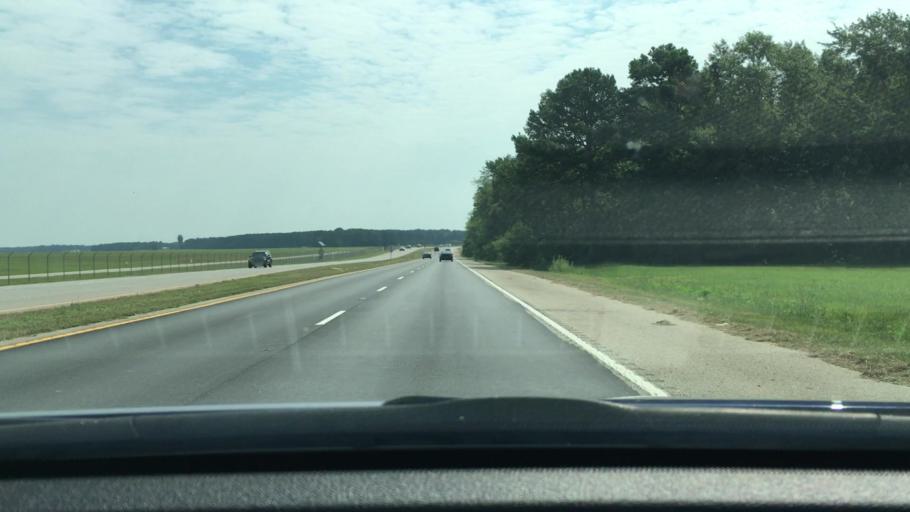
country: US
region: South Carolina
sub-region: Sumter County
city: Cherryvale
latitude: 33.9579
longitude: -80.4807
